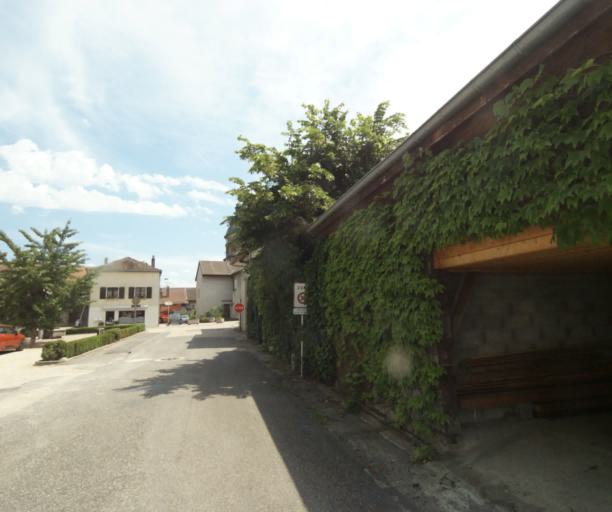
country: FR
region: Rhone-Alpes
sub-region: Departement de la Haute-Savoie
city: Chens-sur-Leman
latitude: 46.3274
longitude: 6.2671
